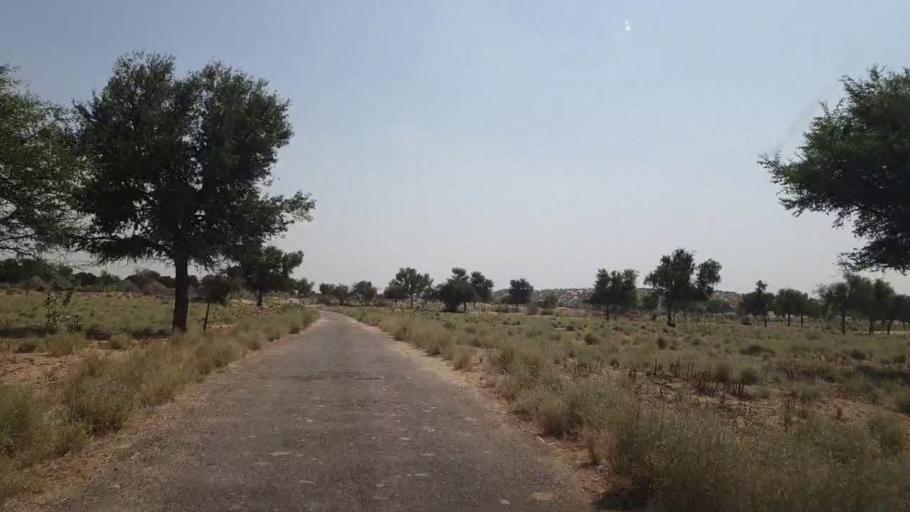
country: PK
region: Sindh
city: Islamkot
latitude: 25.0856
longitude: 70.6738
